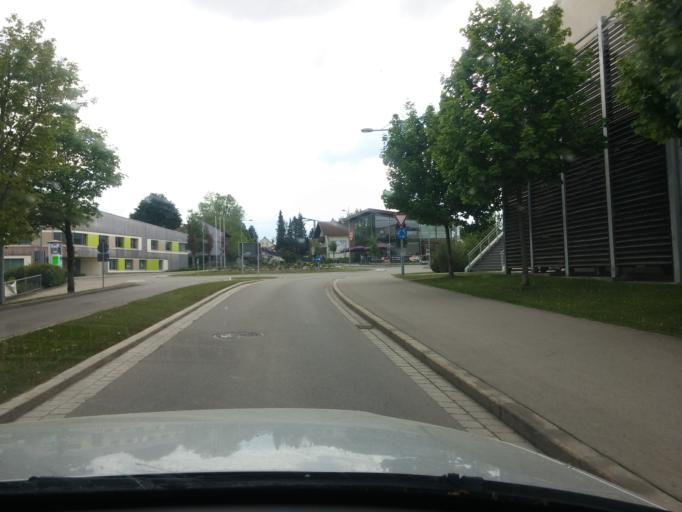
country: DE
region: Bavaria
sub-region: Upper Bavaria
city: Holzkirchen
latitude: 47.8816
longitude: 11.7034
